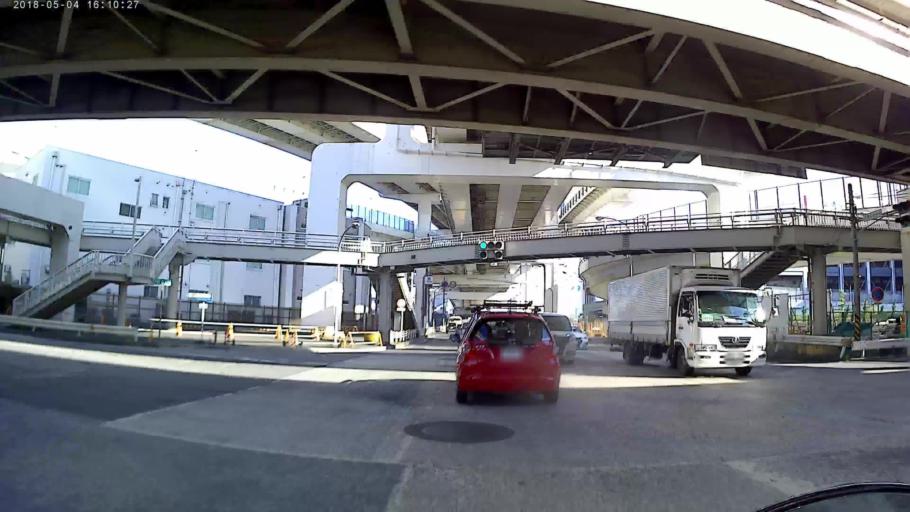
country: JP
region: Kanagawa
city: Yokohama
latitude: 35.4916
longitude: 139.6709
